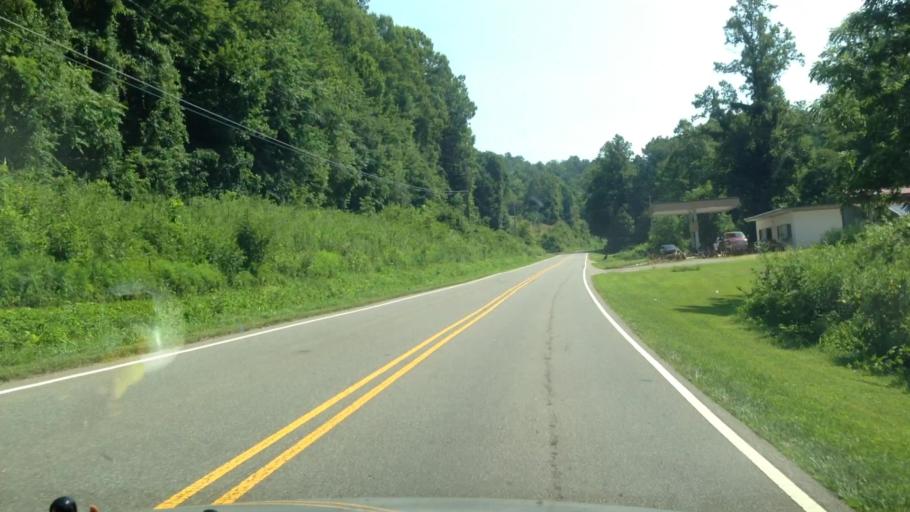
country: US
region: North Carolina
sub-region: Surry County
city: Flat Rock
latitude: 36.5331
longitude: -80.5244
